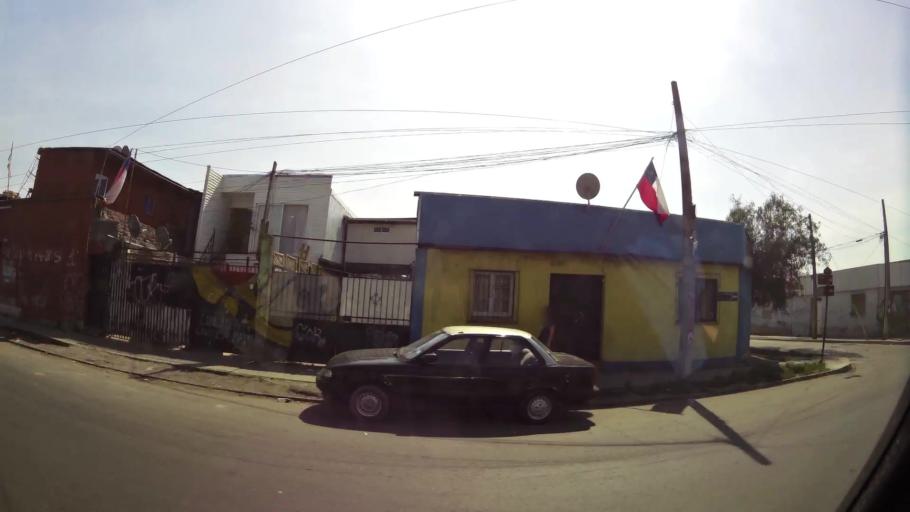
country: CL
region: Santiago Metropolitan
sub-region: Provincia de Santiago
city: Lo Prado
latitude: -33.4290
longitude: -70.7286
